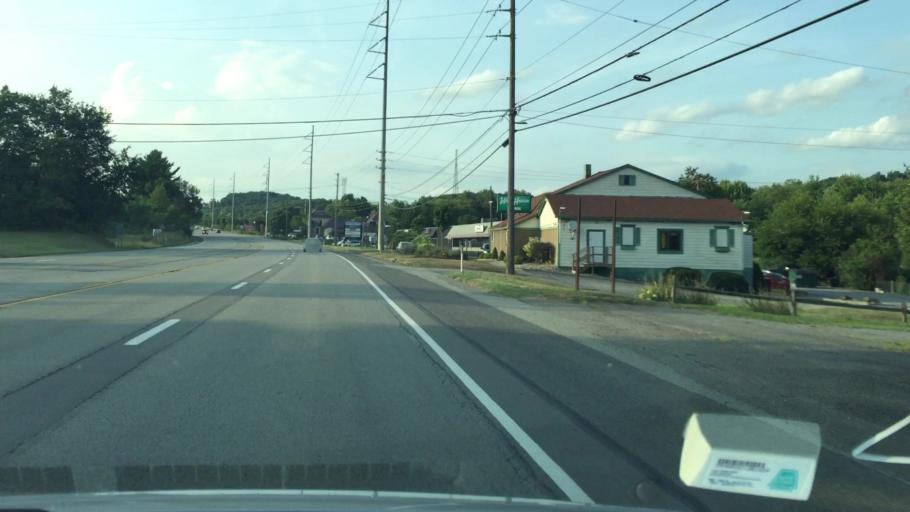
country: US
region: Pennsylvania
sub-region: Butler County
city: Fox Run
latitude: 40.7127
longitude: -80.1038
